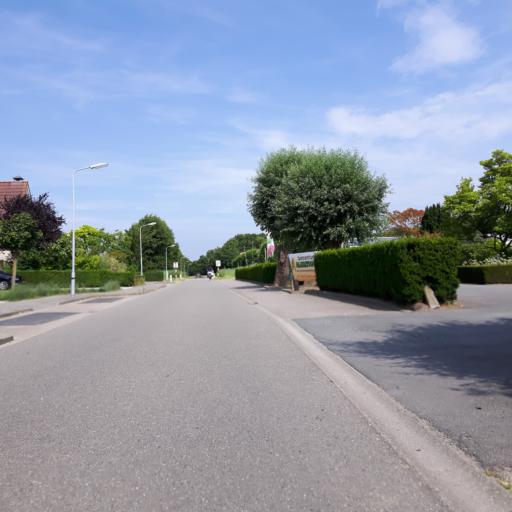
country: NL
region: Zeeland
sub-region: Gemeente Goes
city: Goes
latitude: 51.4905
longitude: 3.9136
